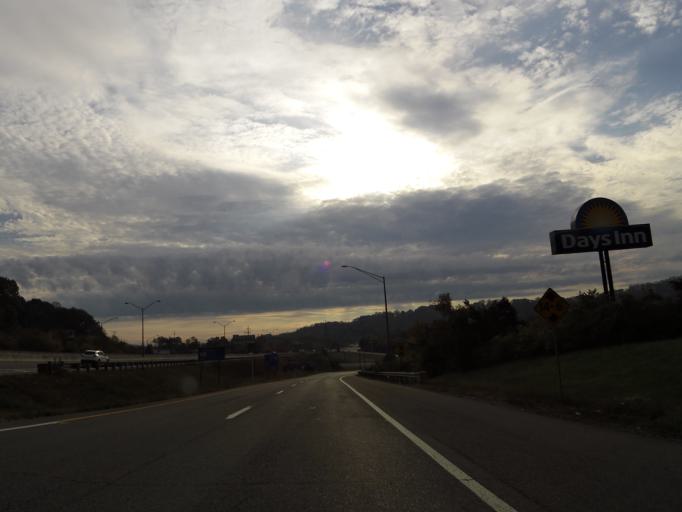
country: US
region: Tennessee
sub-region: Knox County
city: Knoxville
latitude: 36.0114
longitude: -83.8448
